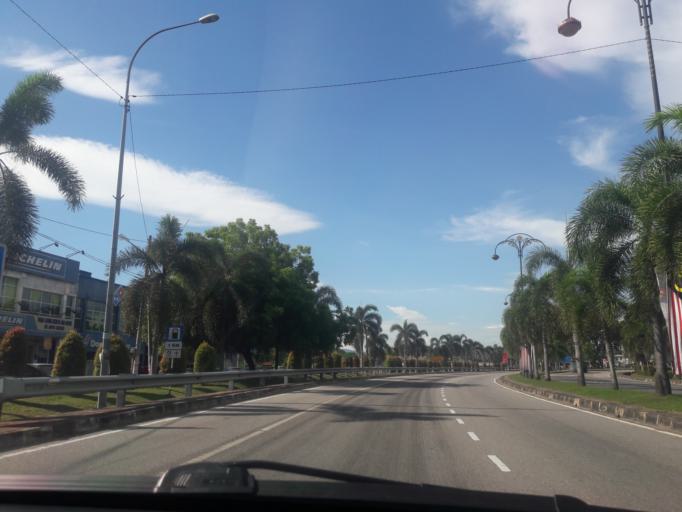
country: MY
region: Kedah
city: Sungai Petani
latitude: 5.6173
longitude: 100.4728
